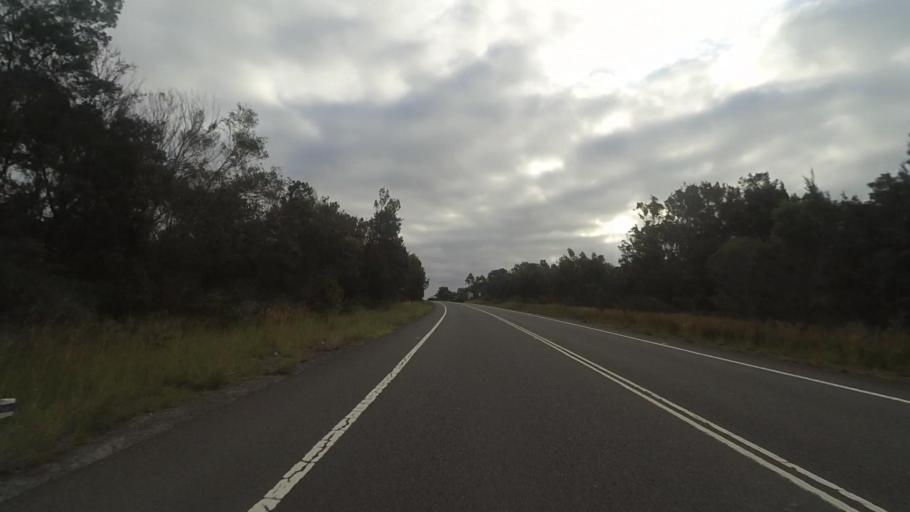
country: AU
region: New South Wales
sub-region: Sutherland Shire
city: Engadine
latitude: -34.0496
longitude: 150.9767
